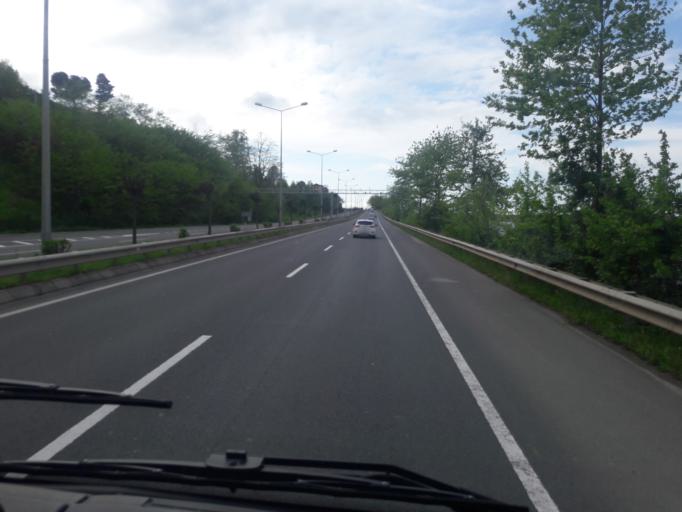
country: TR
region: Giresun
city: Piraziz
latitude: 40.9593
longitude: 38.1081
